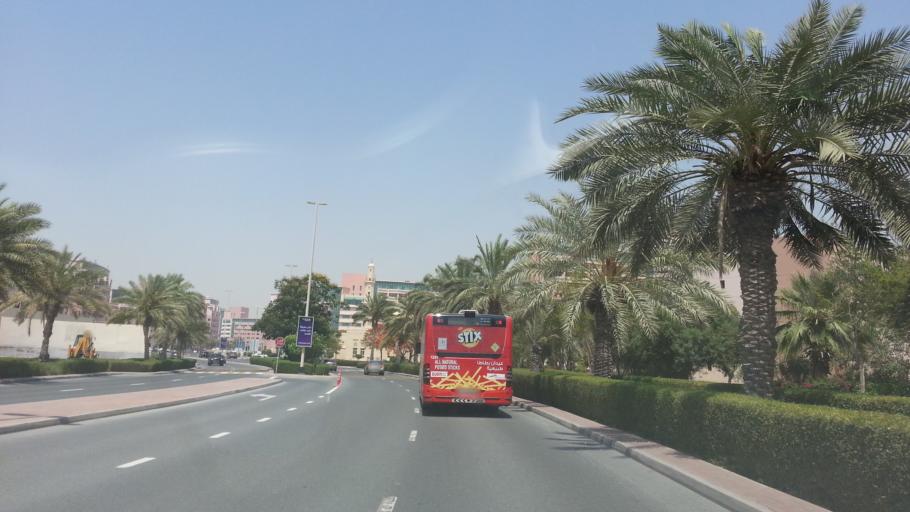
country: AE
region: Dubai
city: Dubai
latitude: 25.0467
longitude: 55.1269
